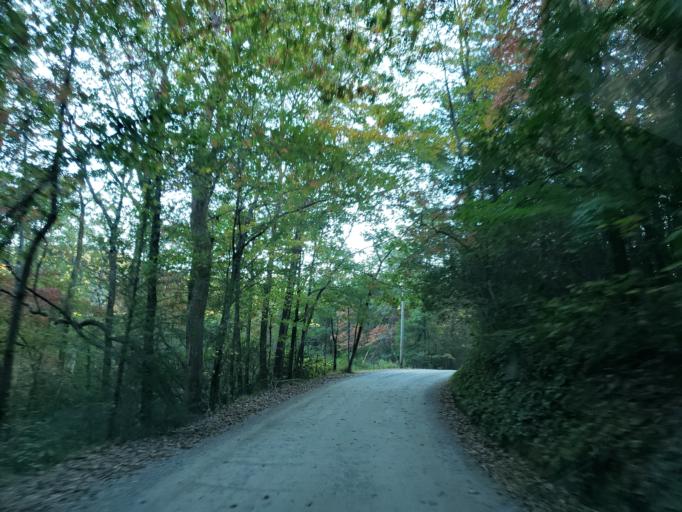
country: US
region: Georgia
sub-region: Gilmer County
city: Ellijay
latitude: 34.6501
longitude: -84.2654
